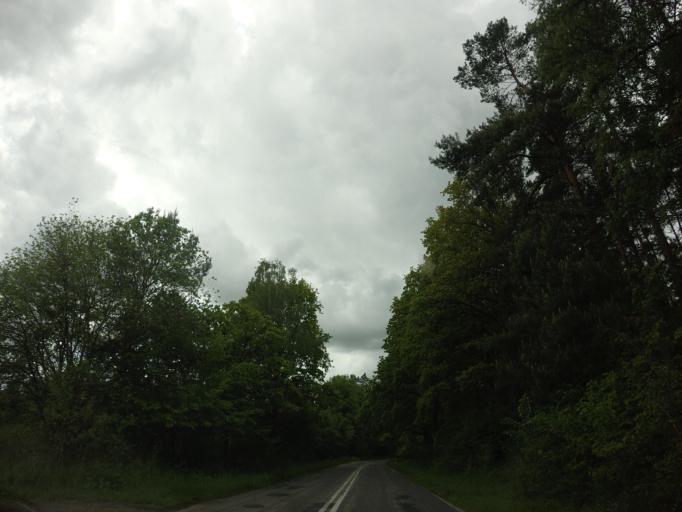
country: PL
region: West Pomeranian Voivodeship
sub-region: Powiat stargardzki
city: Dolice
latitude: 53.2042
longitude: 15.2795
